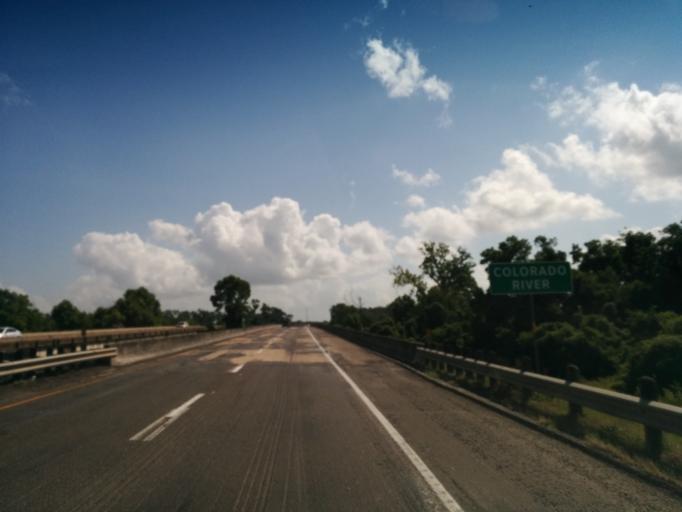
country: US
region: Texas
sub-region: Colorado County
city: Columbus
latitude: 29.6949
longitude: -96.5338
